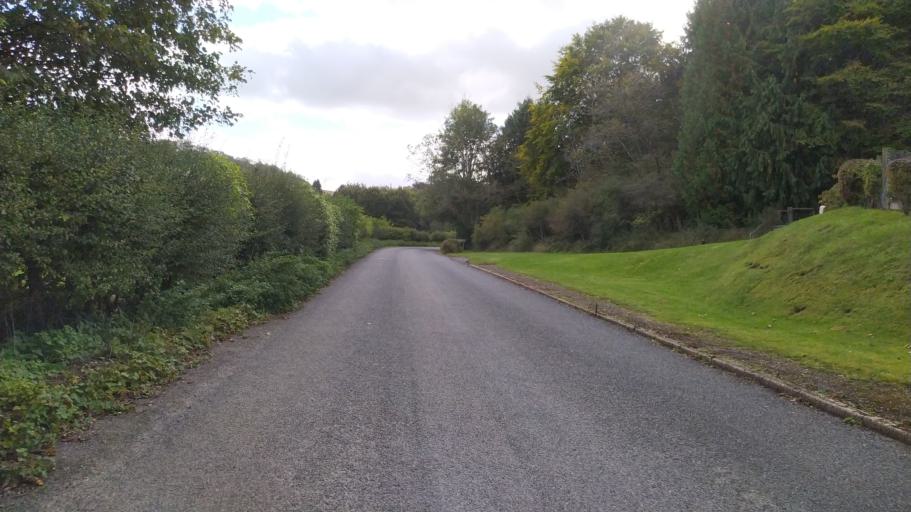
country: GB
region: England
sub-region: Hampshire
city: Highclere
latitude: 51.2805
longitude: -1.3399
